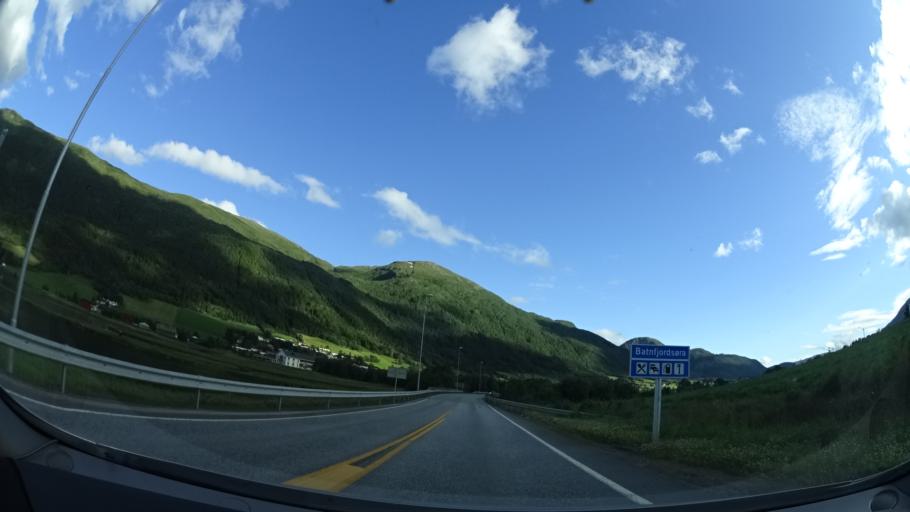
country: NO
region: More og Romsdal
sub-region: Gjemnes
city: Batnfjordsora
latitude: 62.8975
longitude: 7.6763
